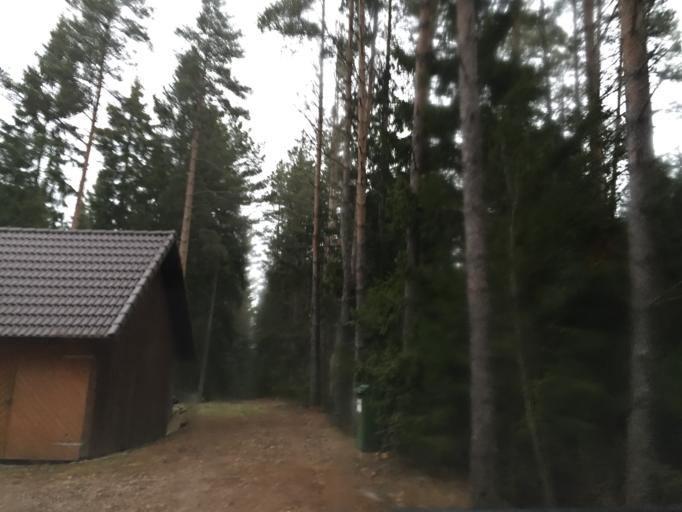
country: EE
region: Saare
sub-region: Kuressaare linn
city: Kuressaare
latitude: 58.5770
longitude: 22.5157
